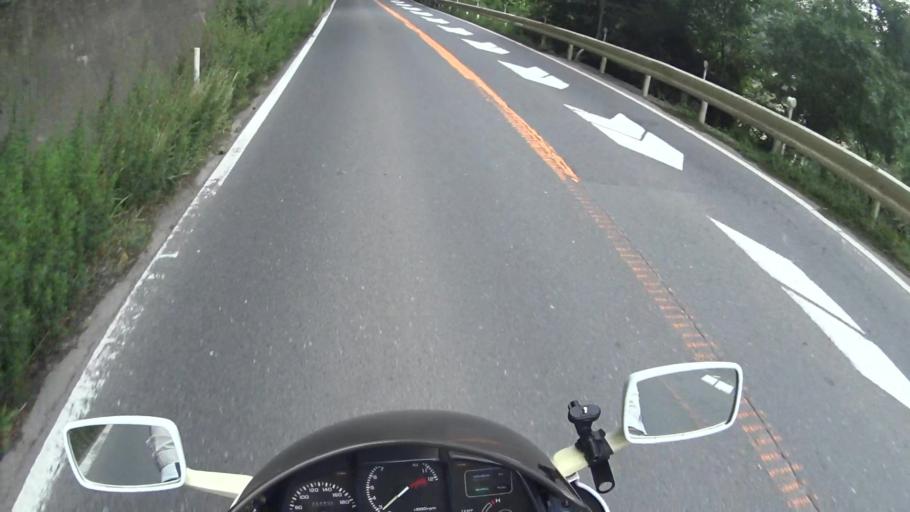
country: JP
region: Nara
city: Nara-shi
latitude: 34.7654
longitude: 135.9009
